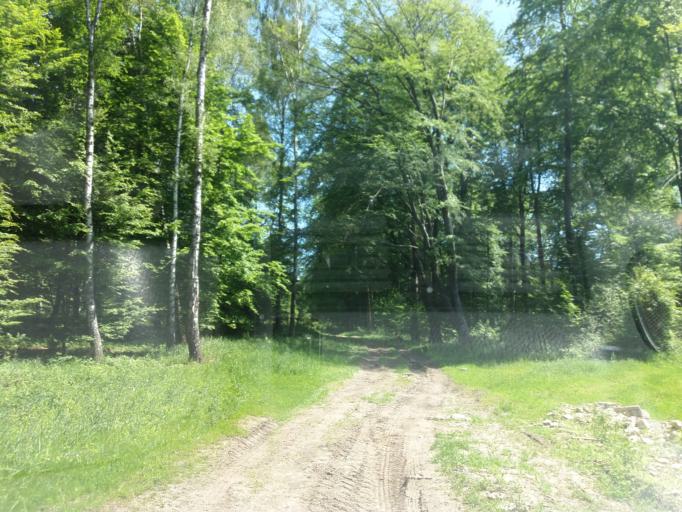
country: PL
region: West Pomeranian Voivodeship
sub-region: Powiat choszczenski
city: Recz
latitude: 53.3176
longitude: 15.5061
